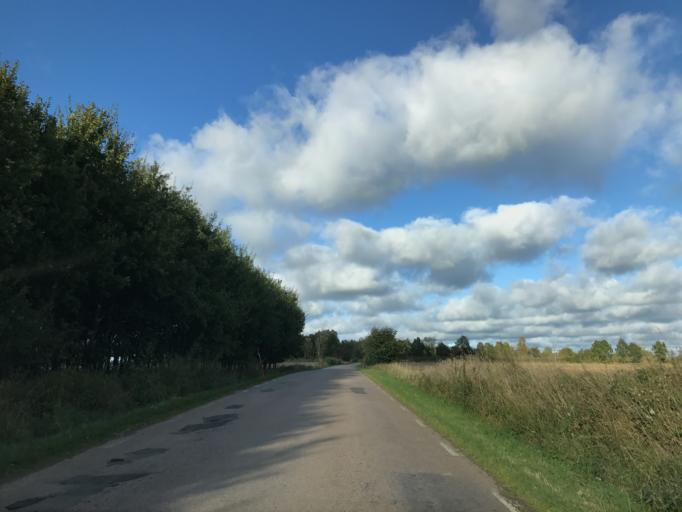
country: SE
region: Skane
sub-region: Svalovs Kommun
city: Kagerod
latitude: 55.9782
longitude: 13.0657
